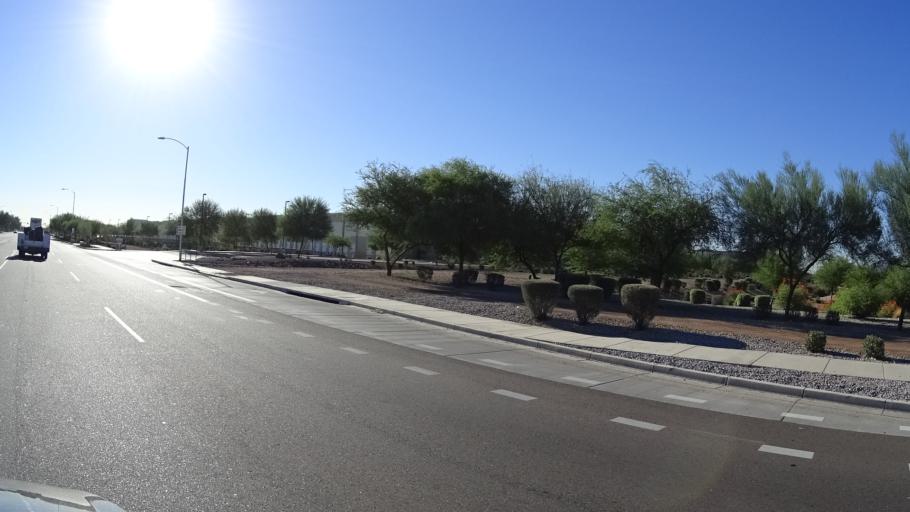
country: US
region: Arizona
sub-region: Maricopa County
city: Laveen
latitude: 33.4224
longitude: -112.1828
